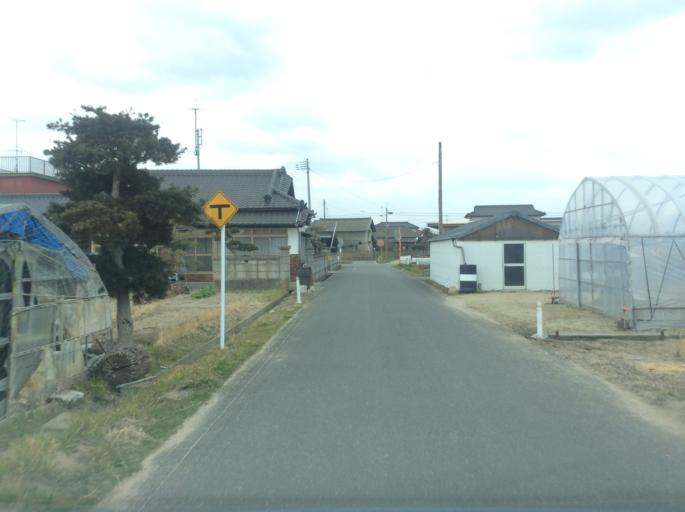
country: JP
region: Fukushima
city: Iwaki
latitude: 37.0802
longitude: 140.9736
